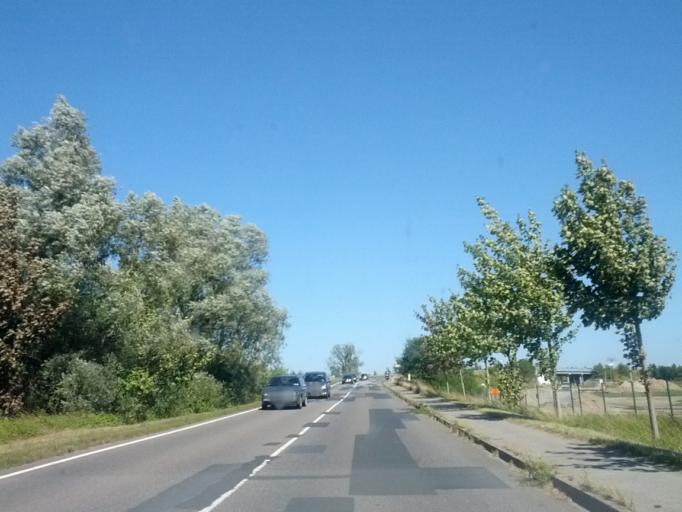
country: DE
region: Mecklenburg-Vorpommern
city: Sagard
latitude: 54.4851
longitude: 13.5772
